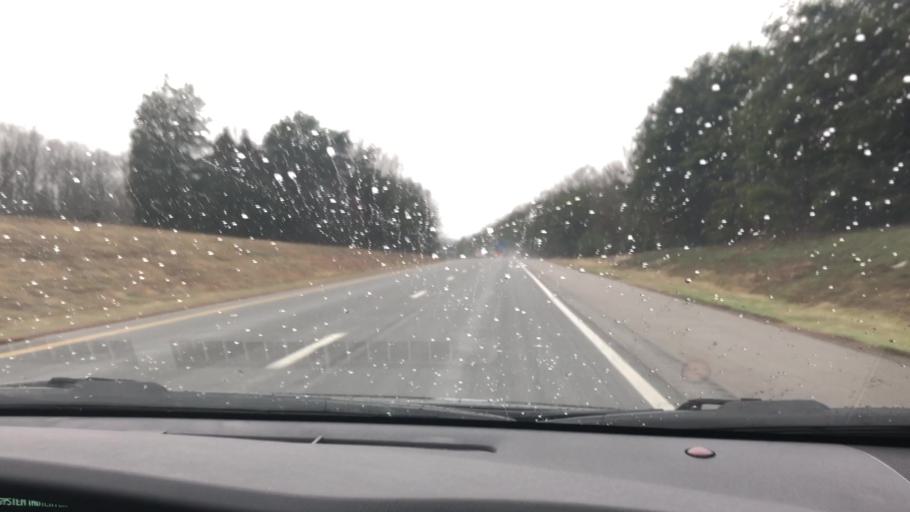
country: US
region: Virginia
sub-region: Fluvanna County
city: Lake Monticello
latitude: 37.9917
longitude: -78.2468
